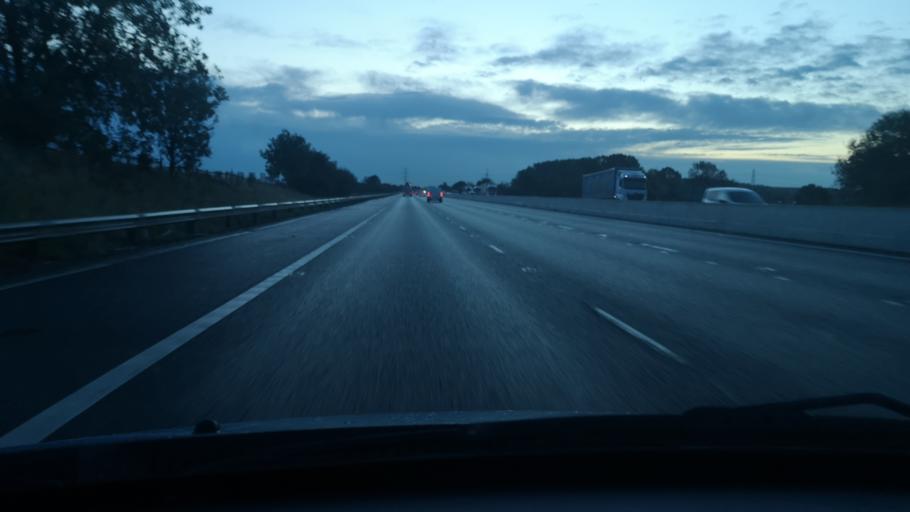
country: GB
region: England
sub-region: City and Borough of Wakefield
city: Knottingley
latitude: 53.6942
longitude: -1.2233
